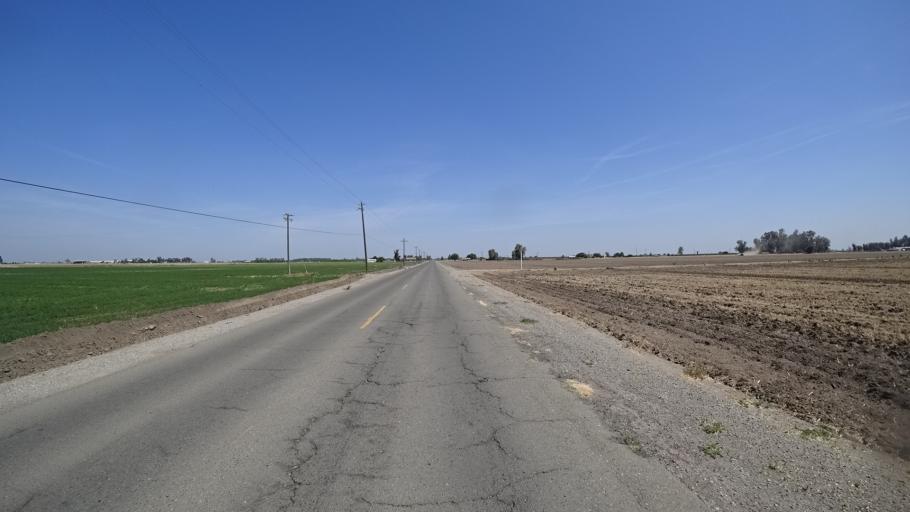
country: US
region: California
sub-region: Fresno County
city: Riverdale
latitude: 36.4050
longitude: -119.8513
